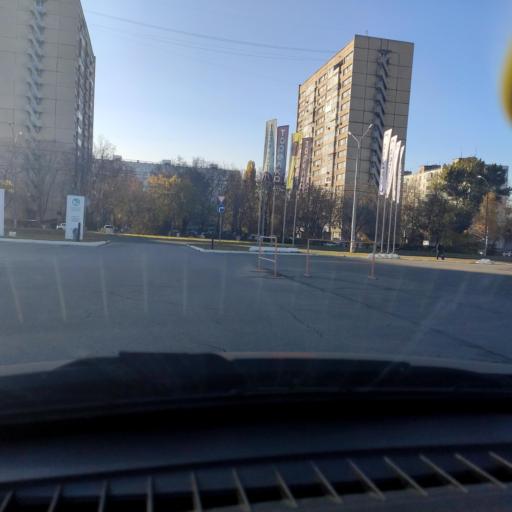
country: RU
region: Samara
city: Tol'yatti
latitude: 53.5153
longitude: 49.2819
